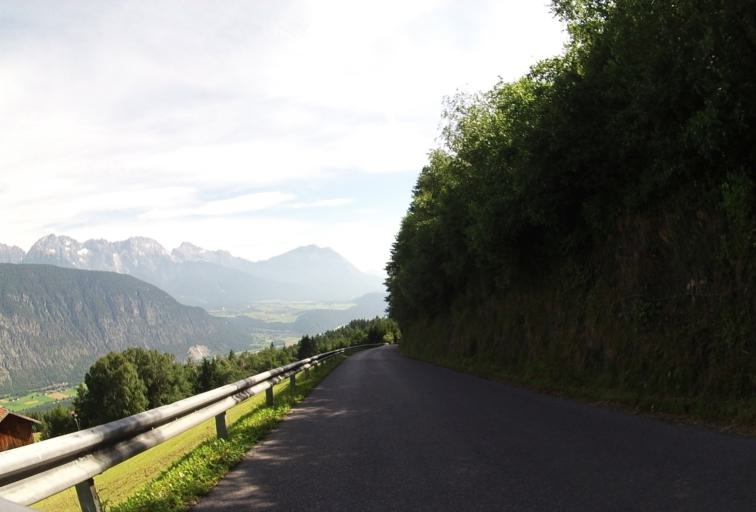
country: AT
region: Tyrol
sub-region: Politischer Bezirk Imst
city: Haiming
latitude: 47.2429
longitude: 10.9000
